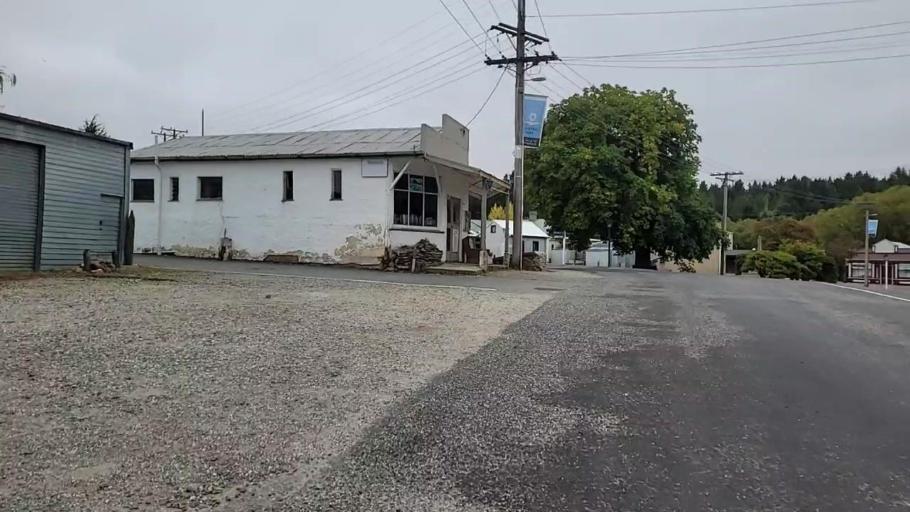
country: NZ
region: Otago
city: Oamaru
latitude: -45.0241
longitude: 170.1463
